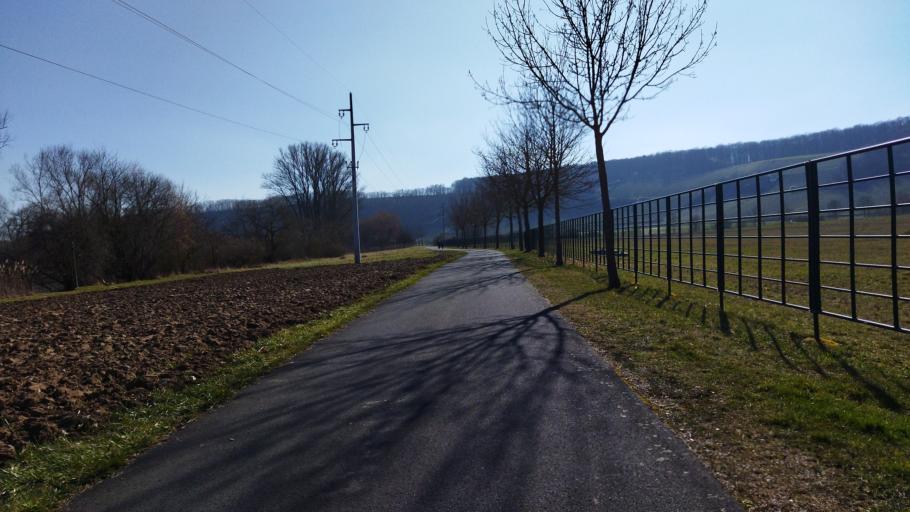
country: DE
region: Bavaria
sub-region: Regierungsbezirk Unterfranken
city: Marktsteft
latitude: 49.6954
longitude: 10.1292
